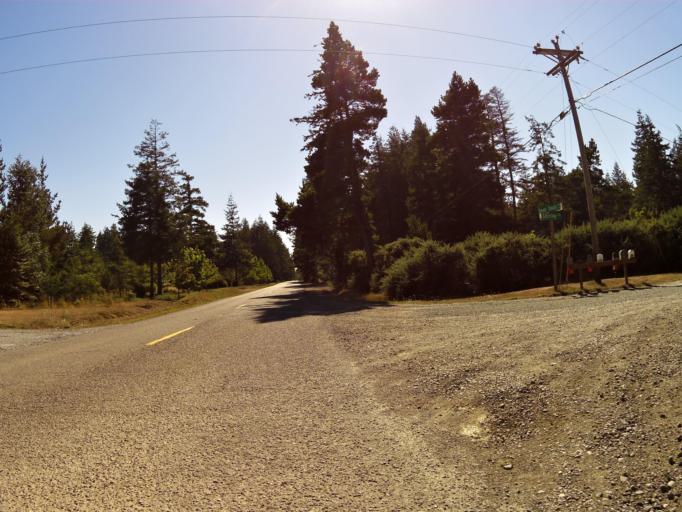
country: US
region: Oregon
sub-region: Coos County
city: Bandon
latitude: 43.1838
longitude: -124.3686
